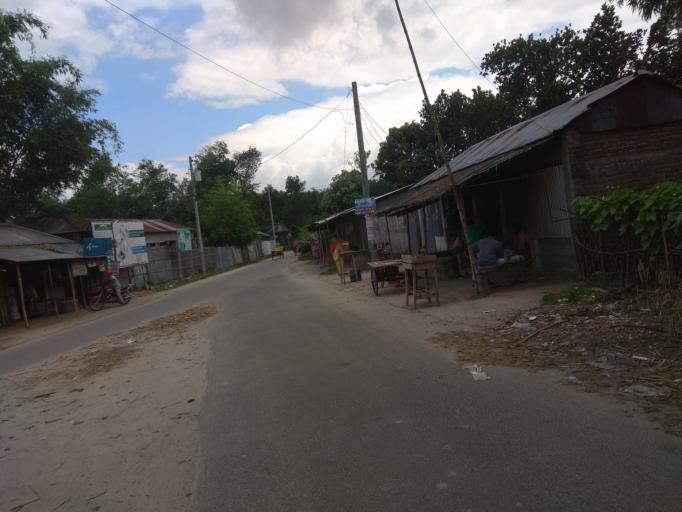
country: IN
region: West Bengal
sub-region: Koch Bihar
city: Haldibari
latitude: 26.1976
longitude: 88.9229
